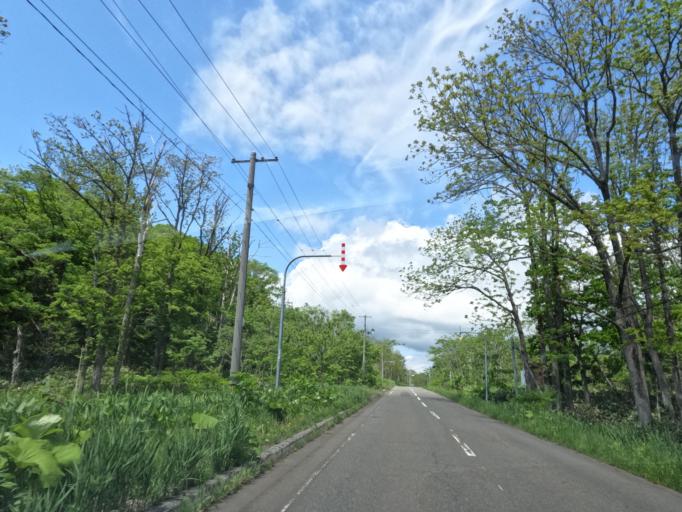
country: JP
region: Hokkaido
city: Tobetsu
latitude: 43.4028
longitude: 141.5820
